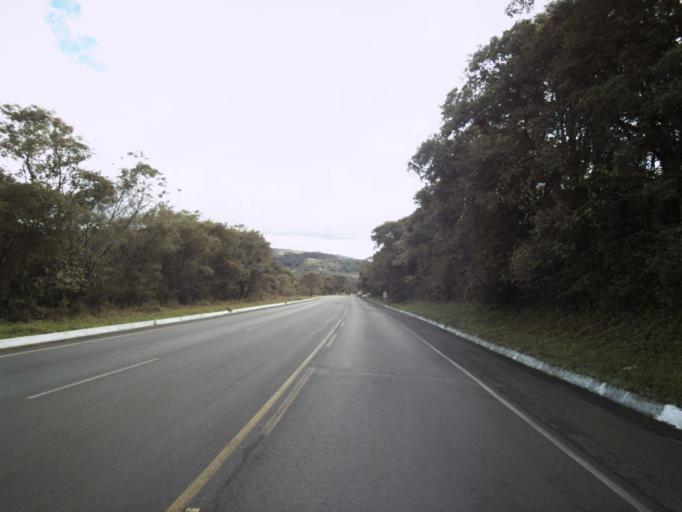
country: BR
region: Santa Catarina
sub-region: Concordia
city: Concordia
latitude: -27.1740
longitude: -51.9090
